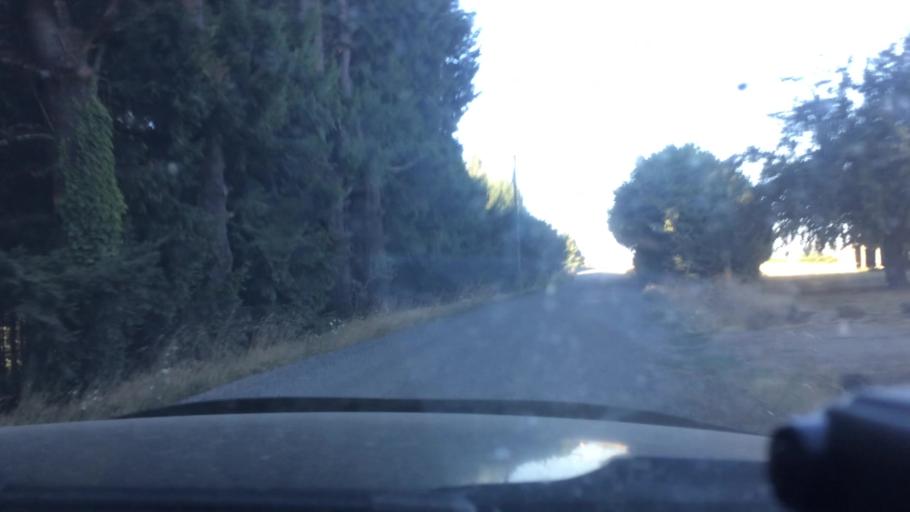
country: US
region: Oregon
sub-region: Yamhill County
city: Newberg
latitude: 45.3707
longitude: -122.9773
